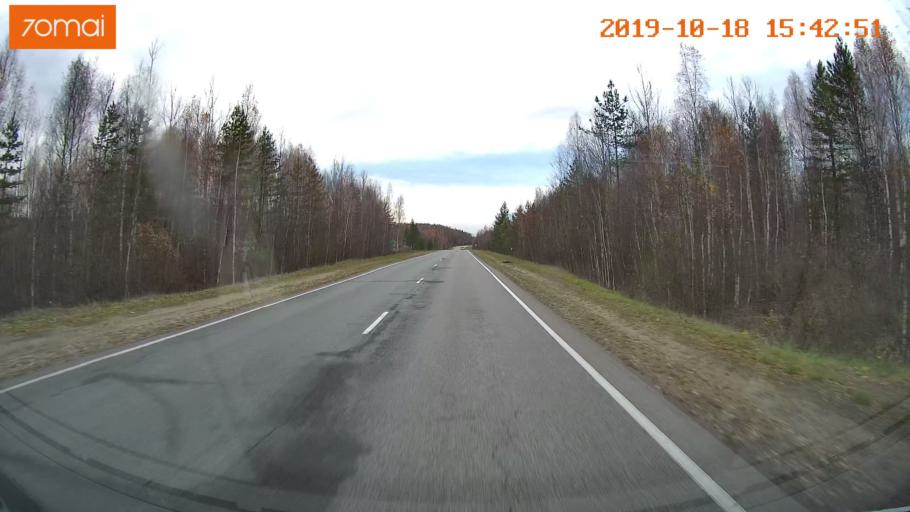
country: RU
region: Vladimir
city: Golovino
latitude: 55.9601
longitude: 40.5610
